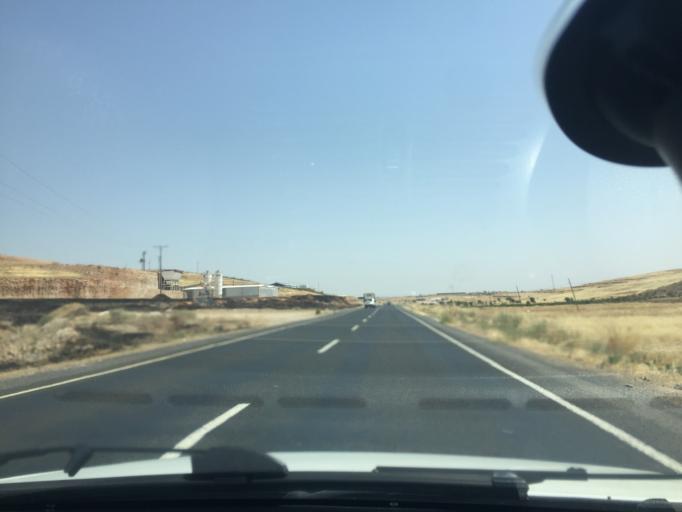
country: TR
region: Mardin
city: Kindirip
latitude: 37.4594
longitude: 41.2380
